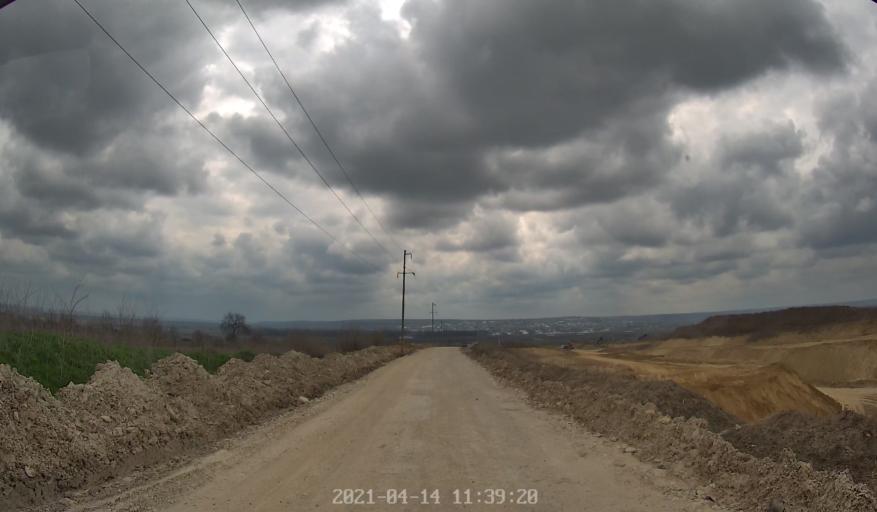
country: MD
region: Criuleni
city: Criuleni
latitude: 47.1680
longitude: 29.1840
